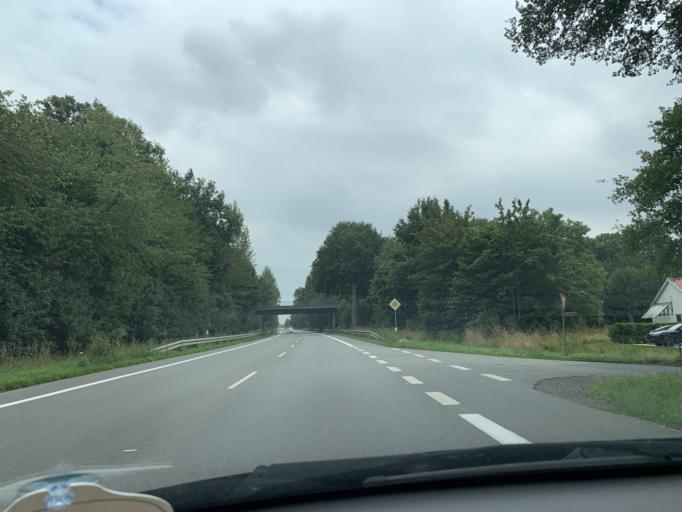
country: DE
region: North Rhine-Westphalia
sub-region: Regierungsbezirk Munster
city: Warendorf
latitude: 51.9424
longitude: 8.0166
